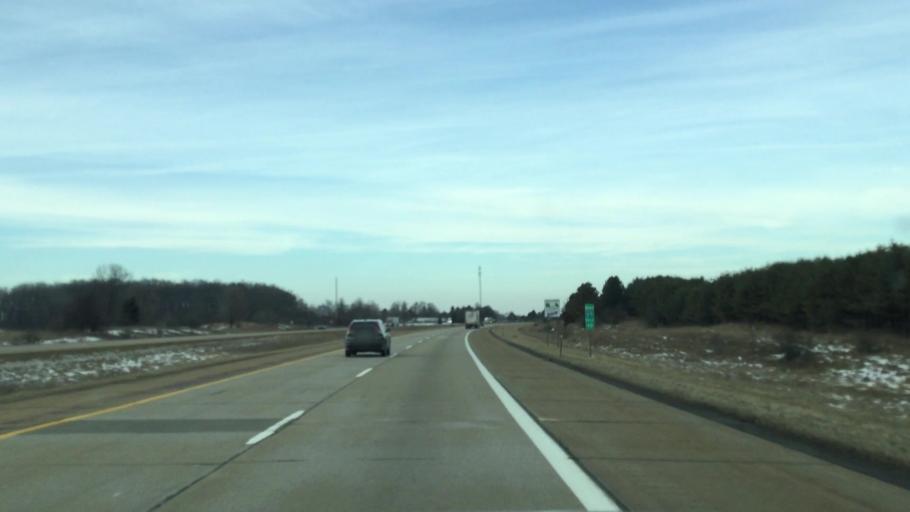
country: US
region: Michigan
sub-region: Calhoun County
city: Marshall
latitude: 42.3219
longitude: -84.9924
